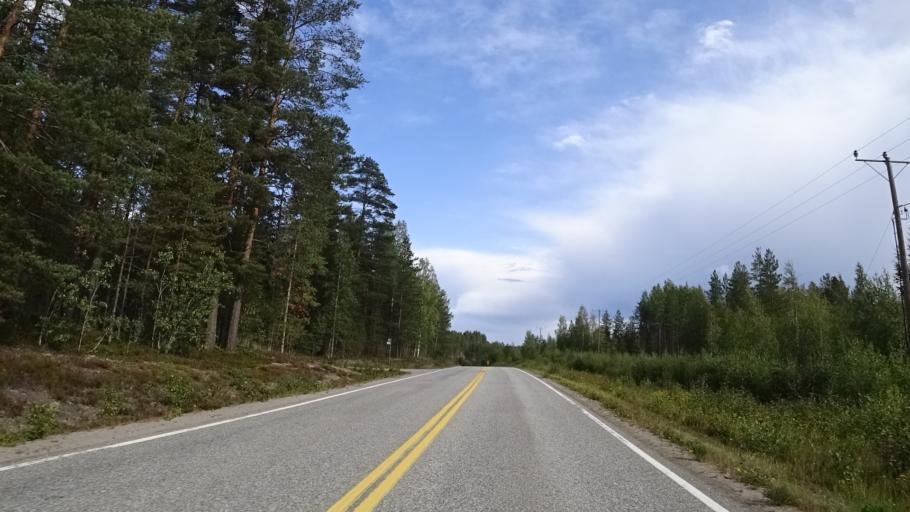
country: FI
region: North Karelia
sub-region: Joensuu
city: Ilomantsi
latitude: 62.6424
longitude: 31.0581
